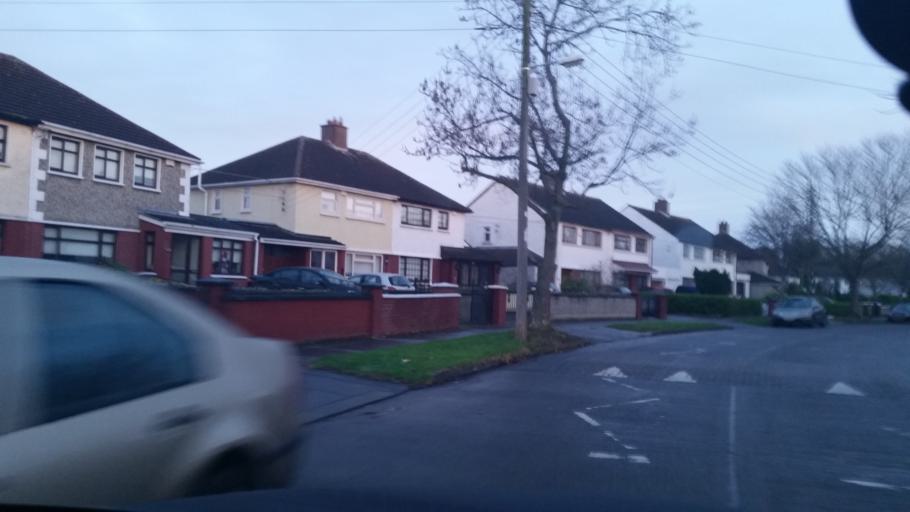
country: IE
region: Leinster
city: Beaumont
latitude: 53.3961
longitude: -6.2518
